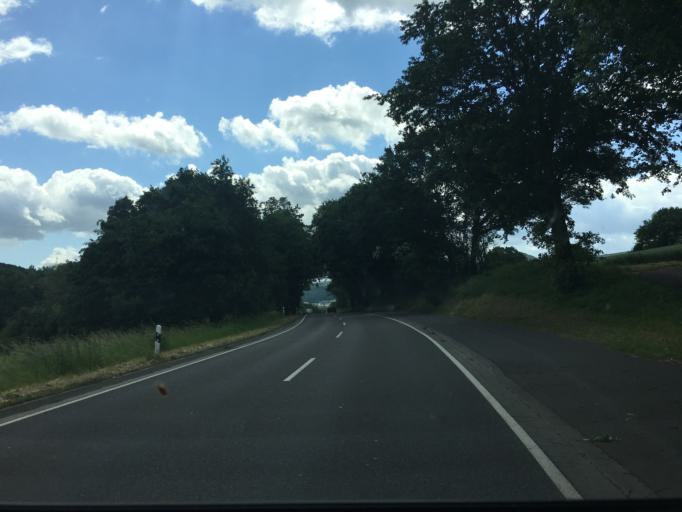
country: DE
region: Rheinland-Pfalz
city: Bad Neuenahr-Ahrweiler
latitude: 50.5554
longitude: 7.1125
